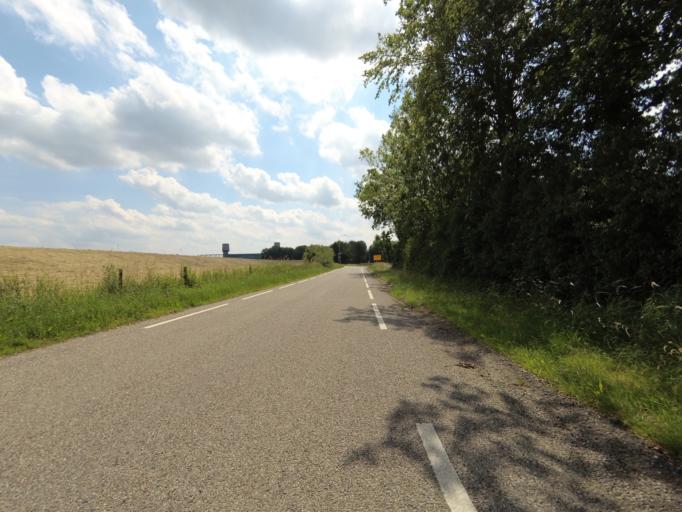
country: NL
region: Utrecht
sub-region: Gemeente Wijk bij Duurstede
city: Wijk bij Duurstede
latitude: 51.9553
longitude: 5.3496
